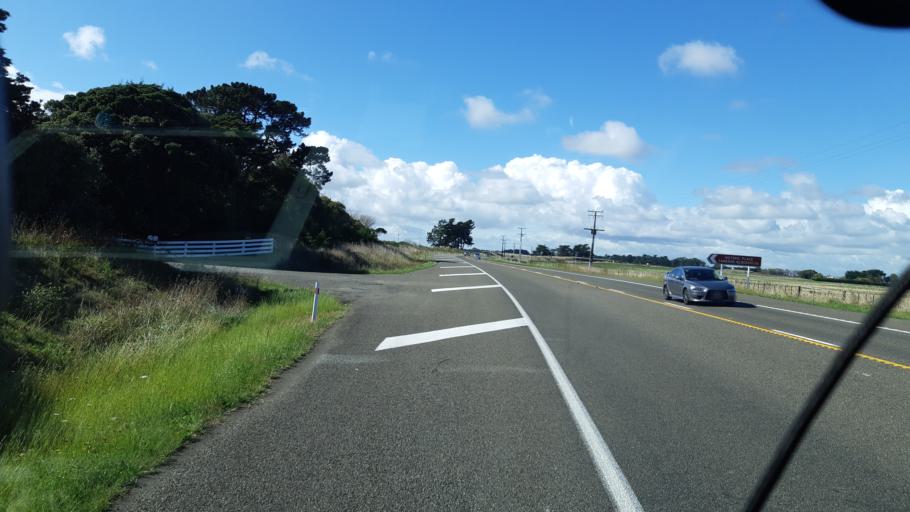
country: NZ
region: Manawatu-Wanganui
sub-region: Wanganui District
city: Wanganui
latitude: -39.9750
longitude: 175.1222
